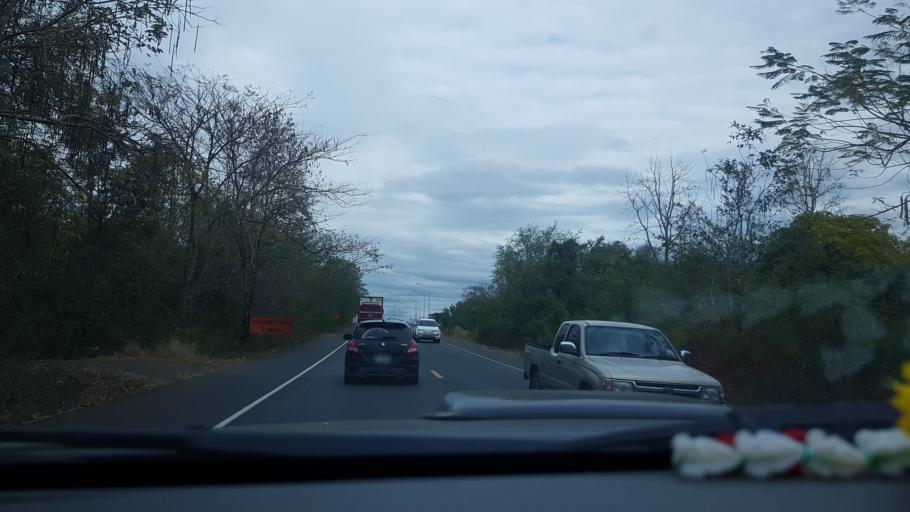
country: TH
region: Phetchabun
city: Phetchabun
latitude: 16.4839
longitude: 101.1369
